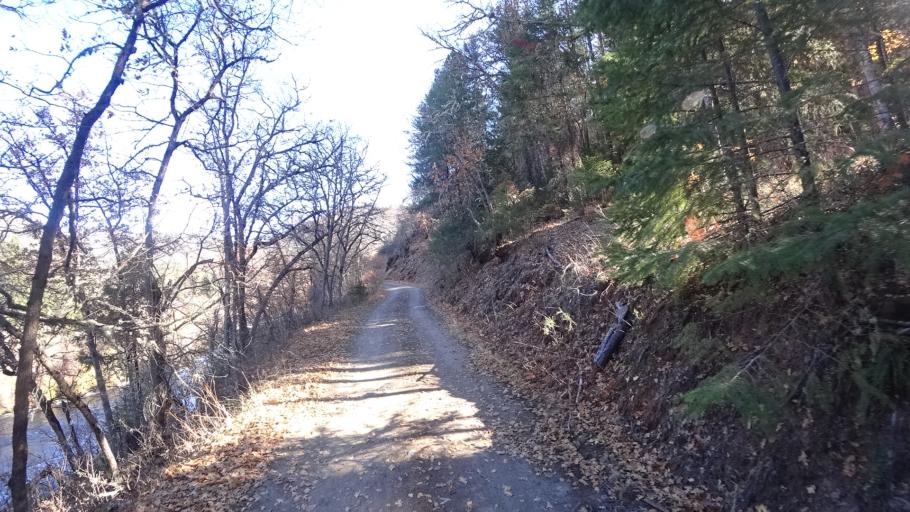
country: US
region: California
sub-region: Siskiyou County
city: Yreka
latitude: 41.8657
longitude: -122.7410
